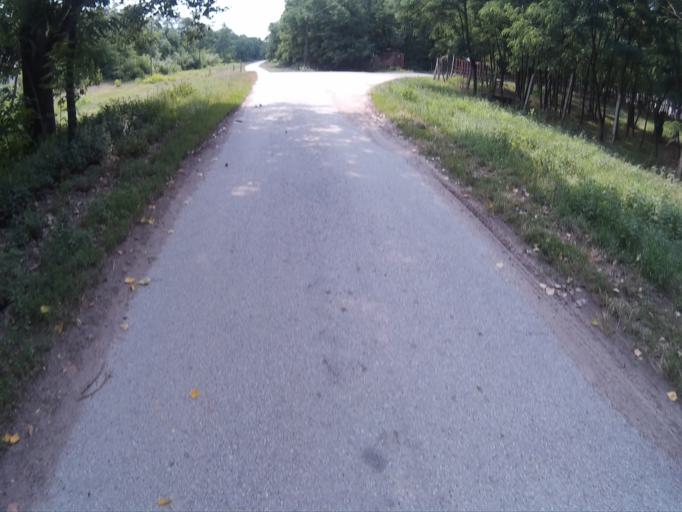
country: HU
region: Veszprem
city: Papa
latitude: 47.2949
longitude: 17.5976
